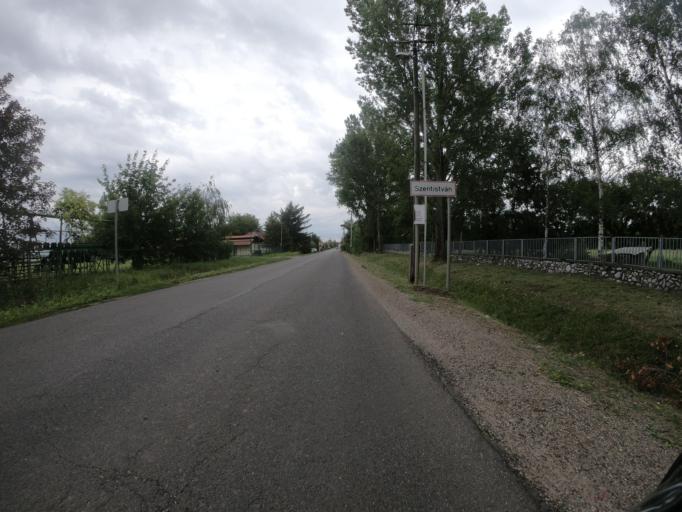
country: HU
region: Borsod-Abauj-Zemplen
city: Szentistvan
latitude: 47.7811
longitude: 20.6441
